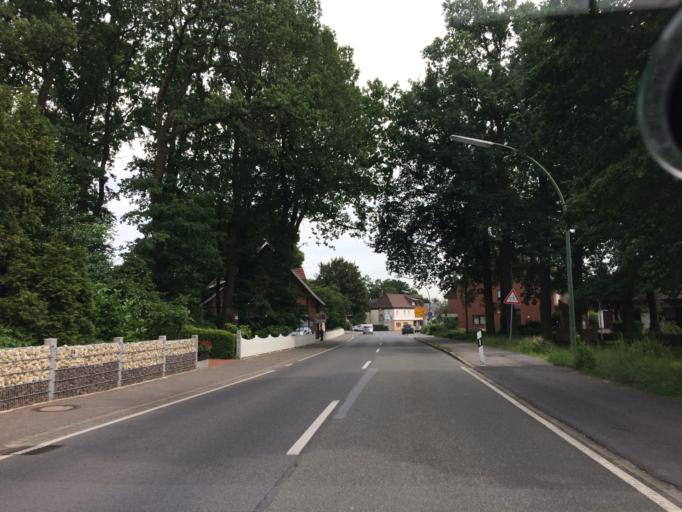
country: DE
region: North Rhine-Westphalia
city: Marl
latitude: 51.7169
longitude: 7.0934
